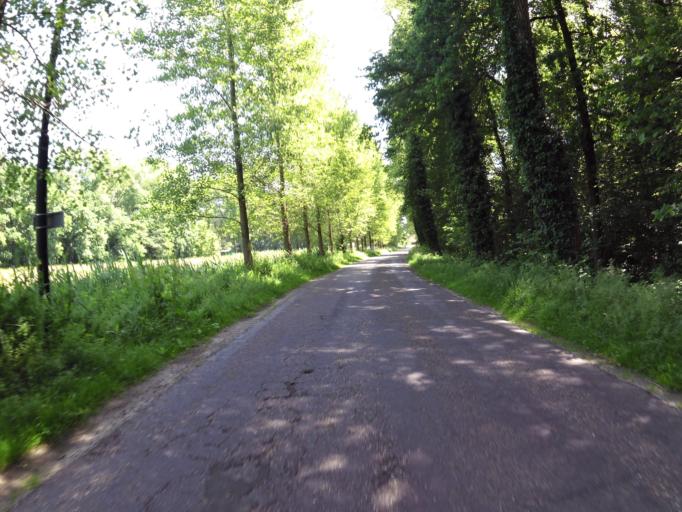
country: NL
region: North Brabant
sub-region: Gemeente Boxtel
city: Boxtel
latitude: 51.5887
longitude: 5.3769
